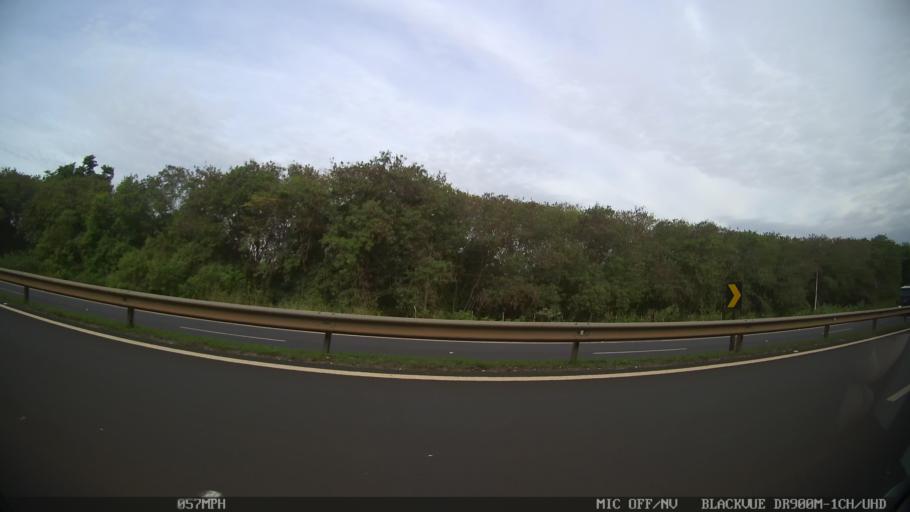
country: BR
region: Sao Paulo
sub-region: Piracicaba
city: Piracicaba
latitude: -22.6976
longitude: -47.5925
